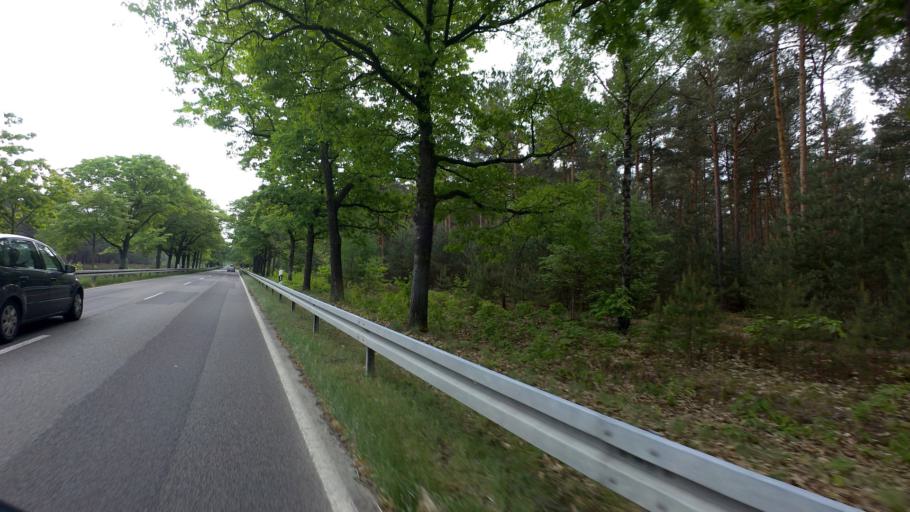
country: DE
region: Brandenburg
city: Drachhausen
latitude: 51.9157
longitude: 14.3503
